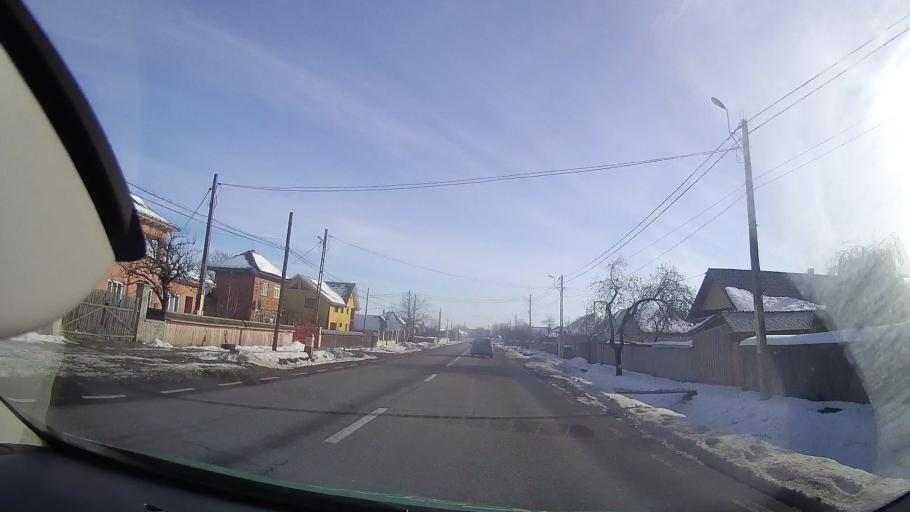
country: RO
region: Neamt
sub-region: Comuna Cracaoani
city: Cracaoani
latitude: 47.0930
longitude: 26.3199
